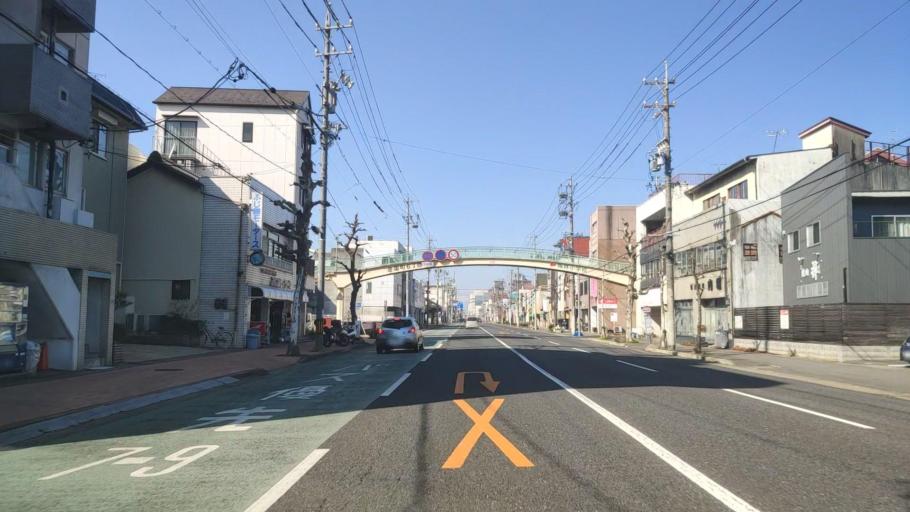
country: JP
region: Gifu
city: Gifu-shi
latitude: 35.4169
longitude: 136.7709
